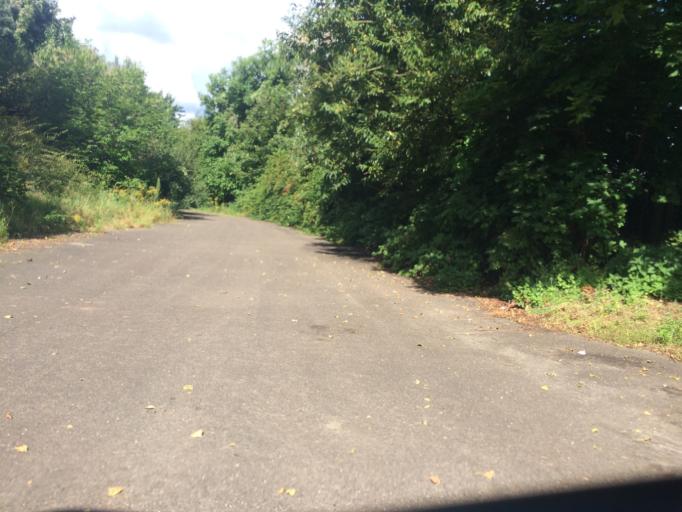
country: DE
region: Berlin
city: Weissensee
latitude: 52.5641
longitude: 13.4569
